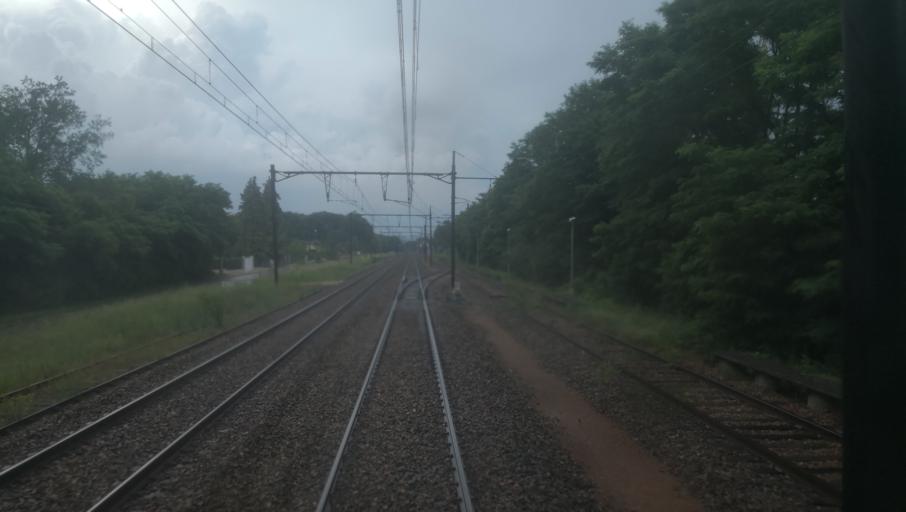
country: FR
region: Centre
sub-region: Departement du Loiret
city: Saint-Cyr-en-Val
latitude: 47.8135
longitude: 1.9468
